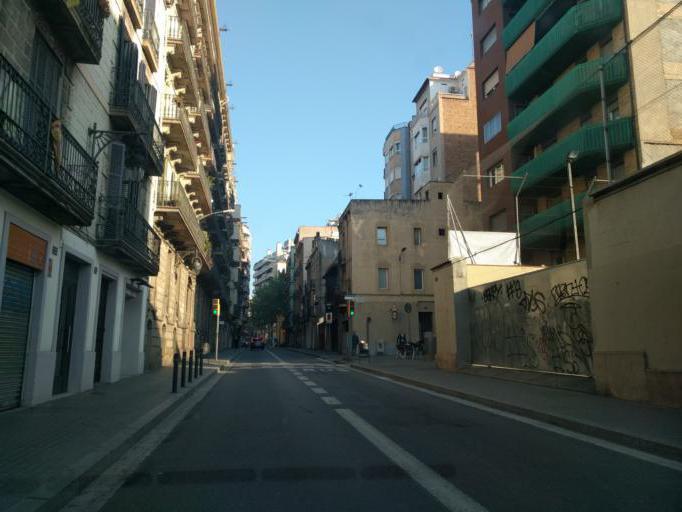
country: ES
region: Catalonia
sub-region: Provincia de Barcelona
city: Gracia
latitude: 41.4047
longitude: 2.1513
